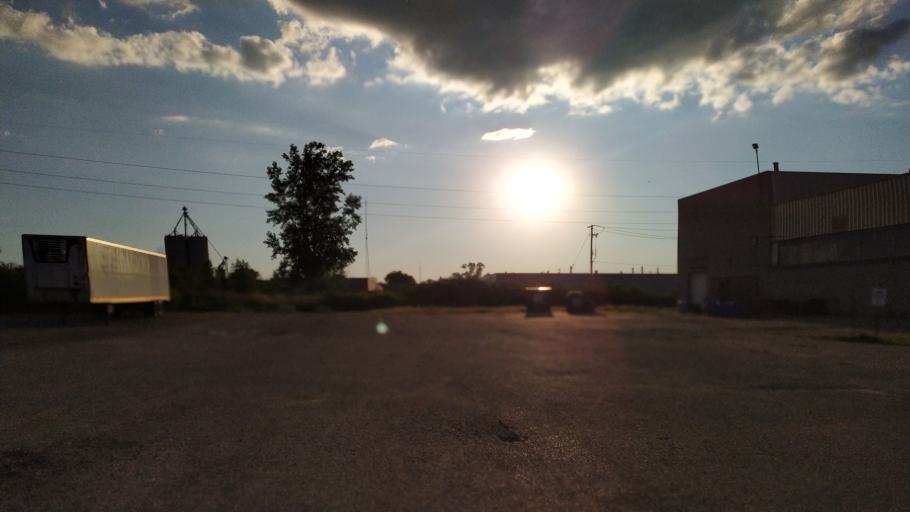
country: CA
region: Ontario
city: Stratford
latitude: 43.3646
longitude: -80.9544
